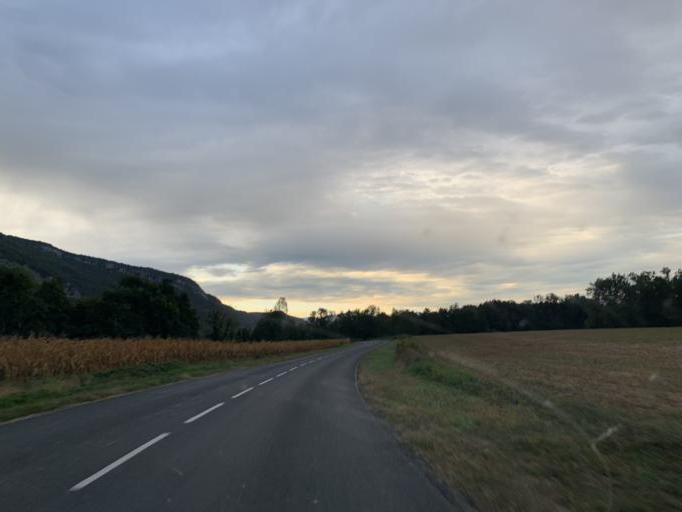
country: FR
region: Rhone-Alpes
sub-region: Departement de l'Isere
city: Les Avenieres
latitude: 45.7022
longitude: 5.5799
